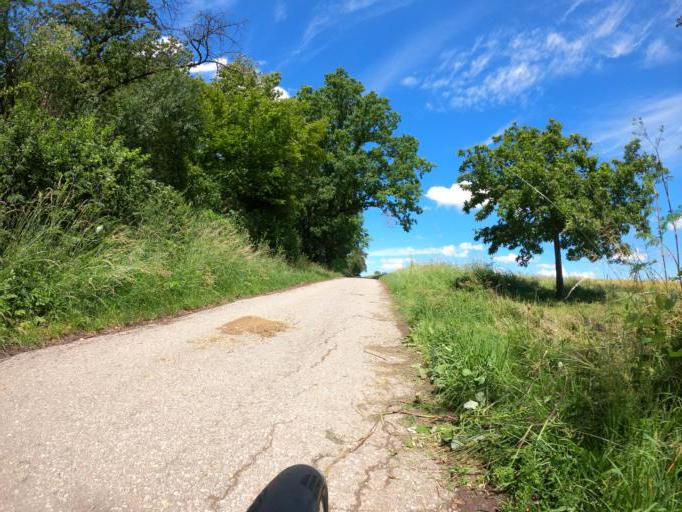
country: DE
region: Baden-Wuerttemberg
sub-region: Regierungsbezirk Stuttgart
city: Markgroningen
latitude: 48.9346
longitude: 9.0882
